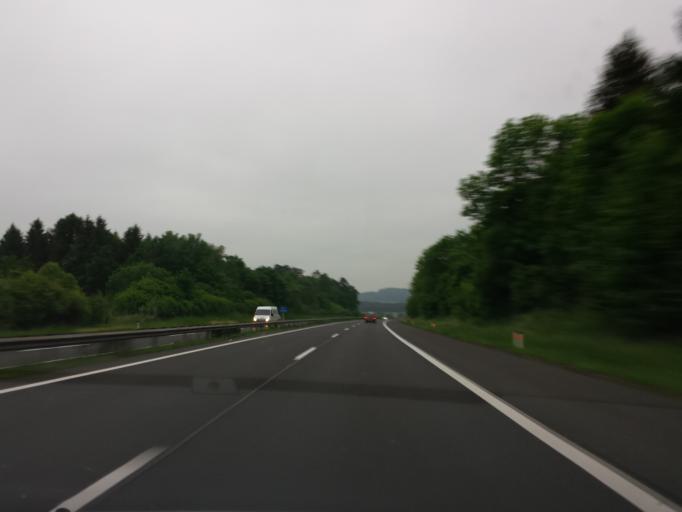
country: AT
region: Styria
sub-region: Politischer Bezirk Hartberg-Fuerstenfeld
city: Hainersdorf
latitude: 47.0987
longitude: 15.9835
